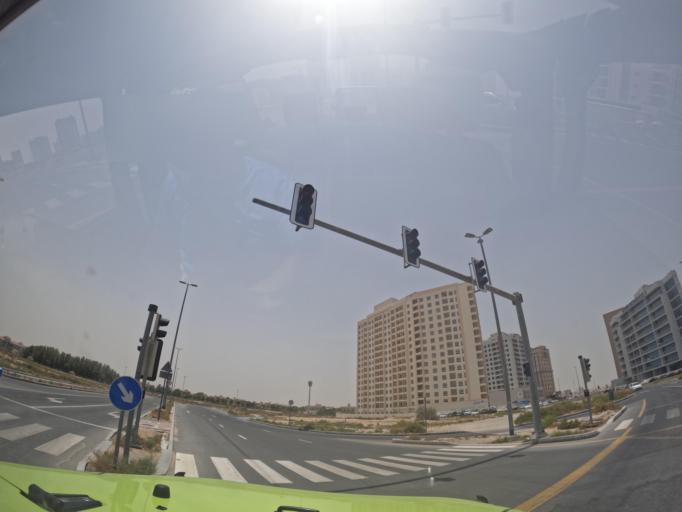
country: AE
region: Dubai
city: Dubai
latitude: 25.0948
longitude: 55.3744
